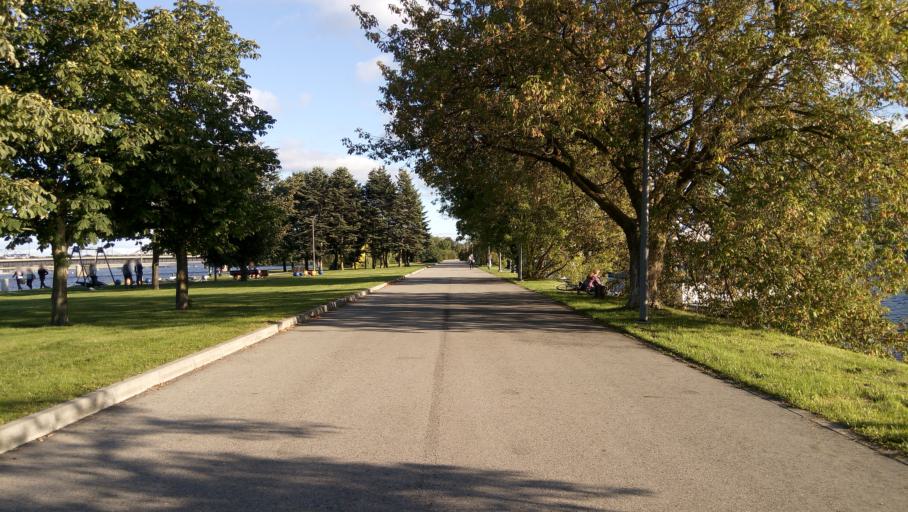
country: LV
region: Riga
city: Riga
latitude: 56.9465
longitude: 24.0943
